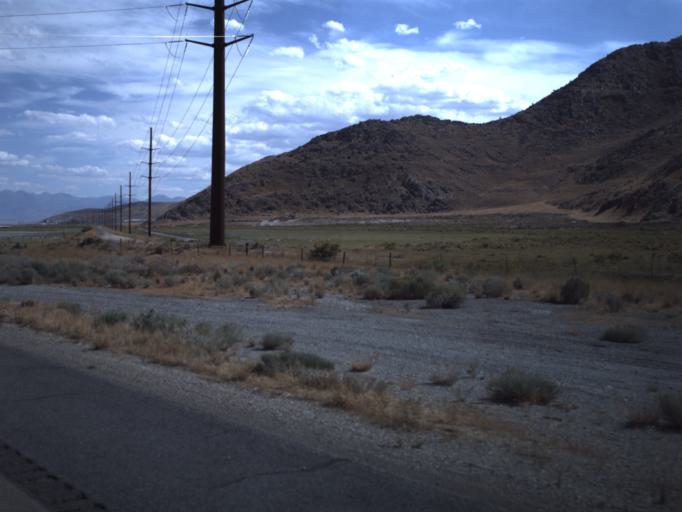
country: US
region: Utah
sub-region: Tooele County
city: Grantsville
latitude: 40.7429
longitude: -112.6321
